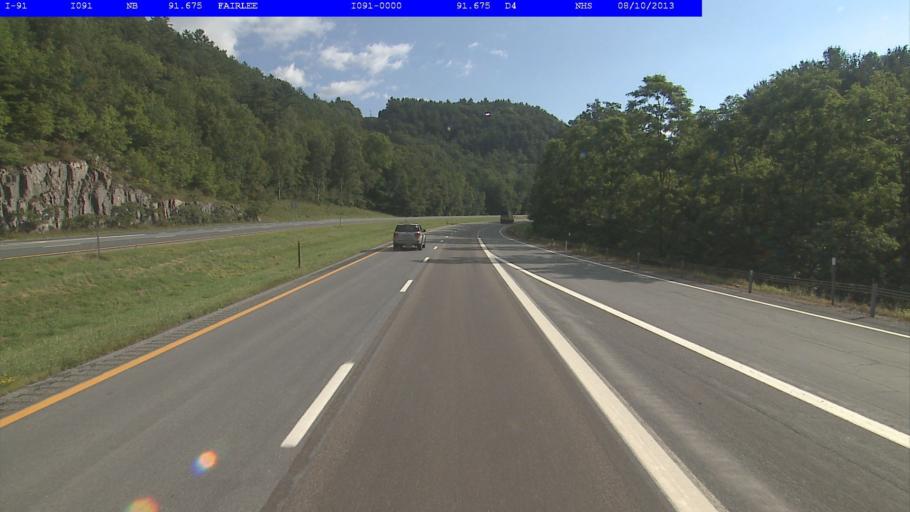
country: US
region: New Hampshire
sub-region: Grafton County
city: Orford
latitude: 43.9067
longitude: -72.1500
